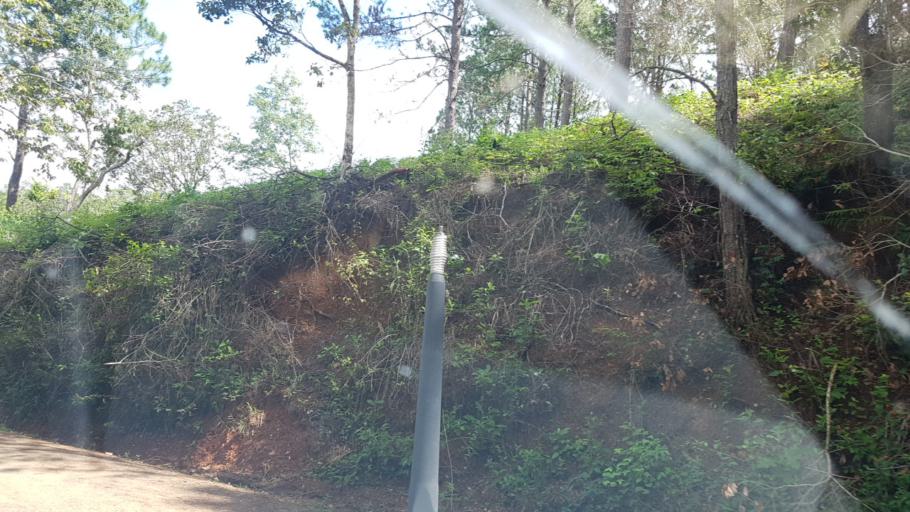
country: NI
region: Nueva Segovia
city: Ciudad Antigua
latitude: 13.6521
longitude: -86.2370
